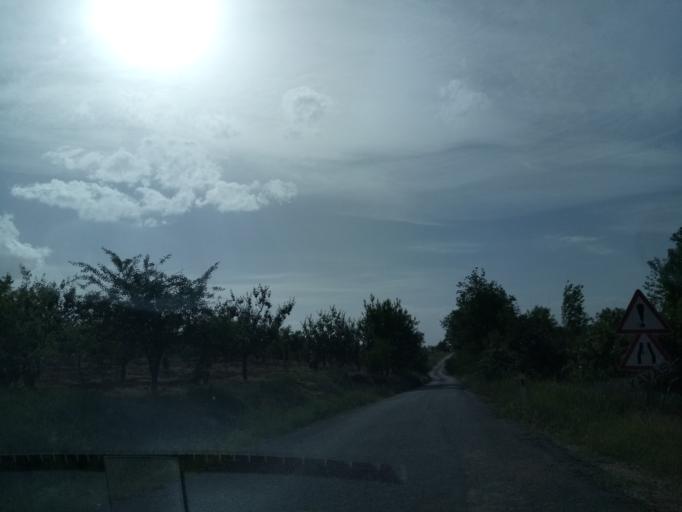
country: TR
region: Konya
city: Ahirli
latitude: 37.2810
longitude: 32.1921
